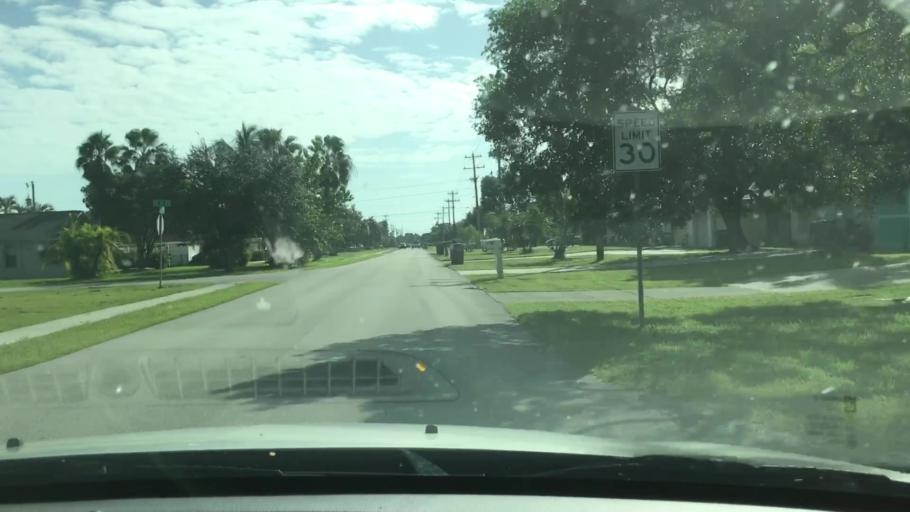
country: US
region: Florida
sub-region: Lee County
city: Lochmoor Waterway Estates
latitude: 26.6379
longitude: -81.9522
